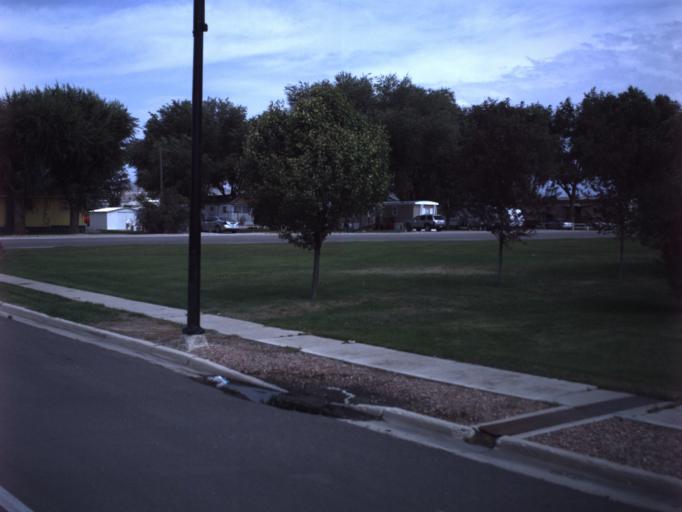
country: US
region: Utah
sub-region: Sanpete County
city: Gunnison
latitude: 39.1580
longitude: -111.8182
